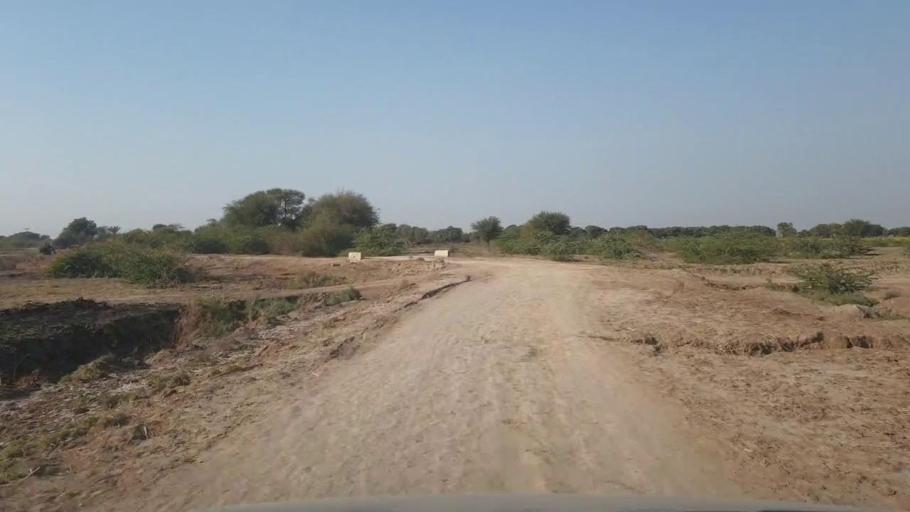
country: PK
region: Sindh
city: Chambar
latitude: 25.3012
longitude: 68.8624
